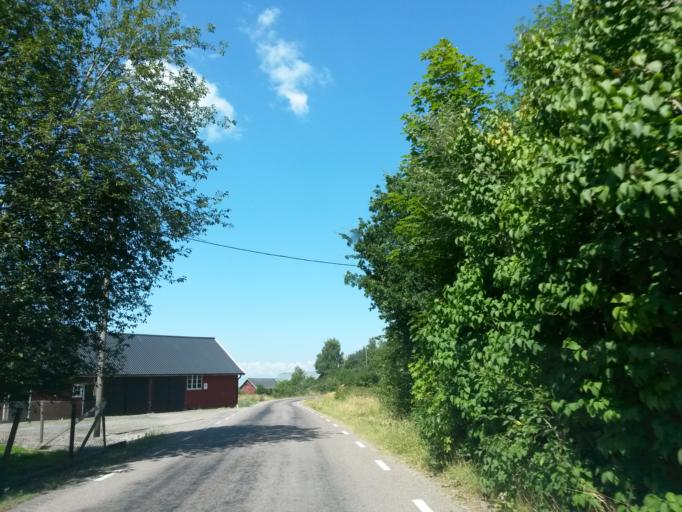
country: SE
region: Vaestra Goetaland
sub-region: Grastorps Kommun
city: Graestorp
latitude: 58.3401
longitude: 12.7615
